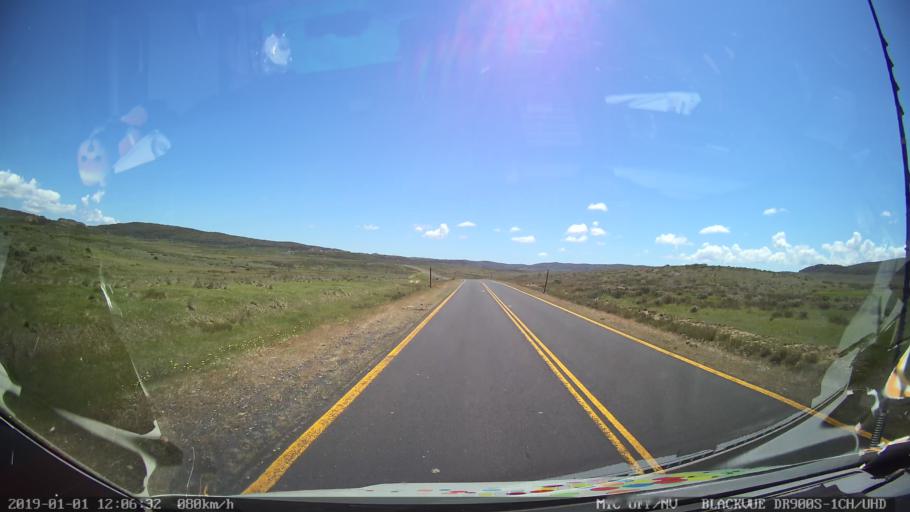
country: AU
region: New South Wales
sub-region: Snowy River
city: Jindabyne
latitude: -35.8438
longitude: 148.4915
